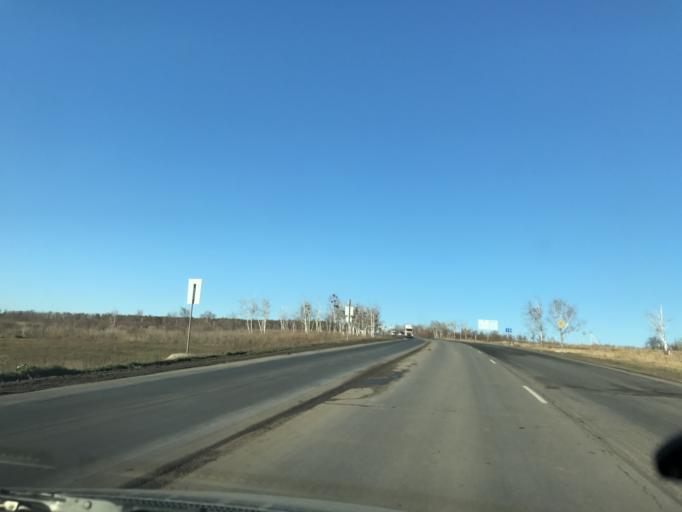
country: RU
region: Rostov
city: Kagal'nitskaya
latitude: 46.8875
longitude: 40.1410
